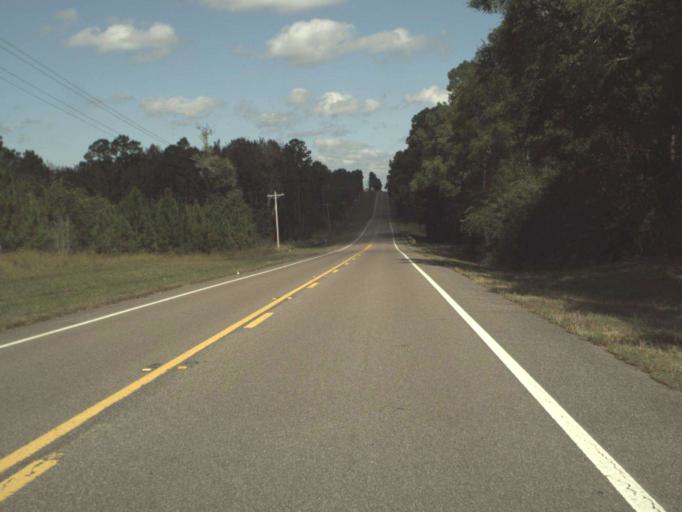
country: US
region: Florida
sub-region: Walton County
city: DeFuniak Springs
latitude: 30.9005
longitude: -86.1302
